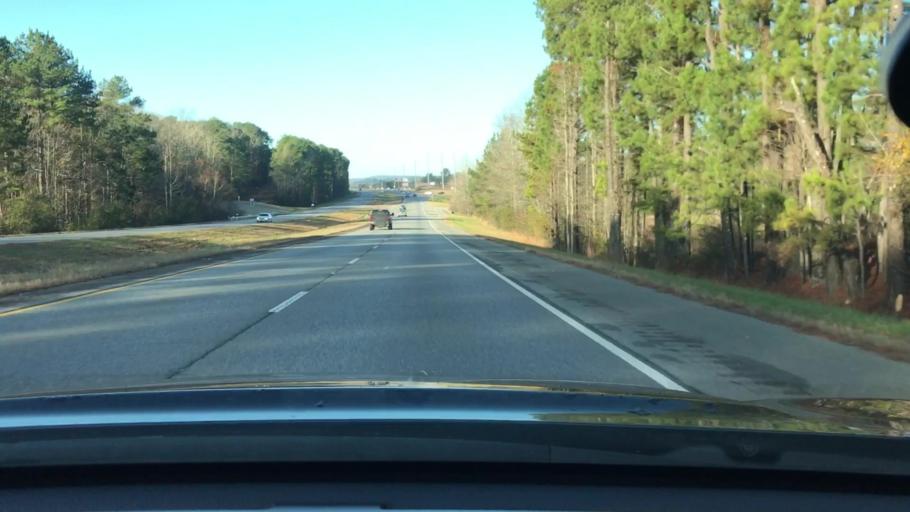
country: US
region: Alabama
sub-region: Shelby County
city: Chelsea
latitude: 33.3511
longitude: -86.6025
